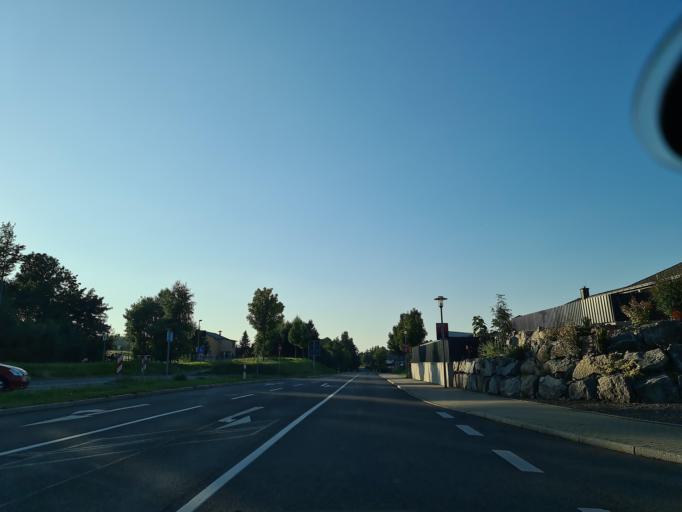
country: DE
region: Saxony
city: Olbernhau
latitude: 50.6572
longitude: 13.3359
